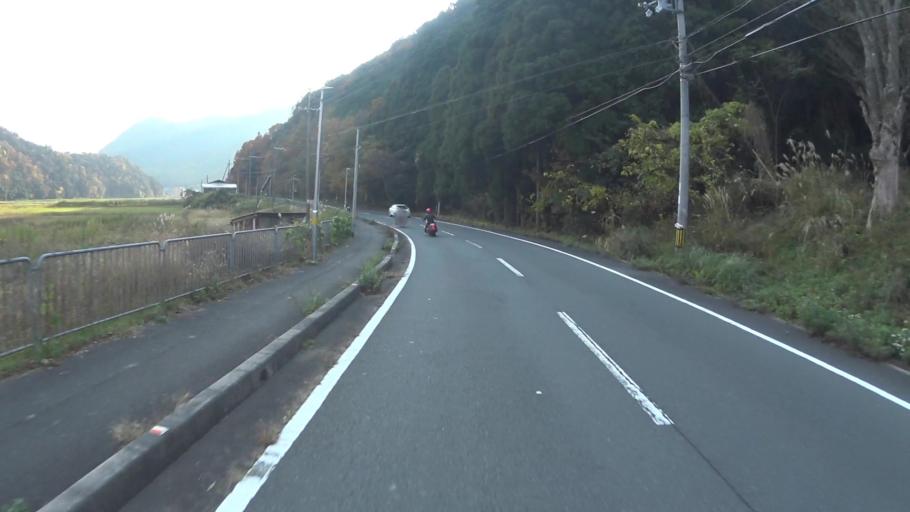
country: JP
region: Kyoto
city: Maizuru
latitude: 35.5063
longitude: 135.4362
